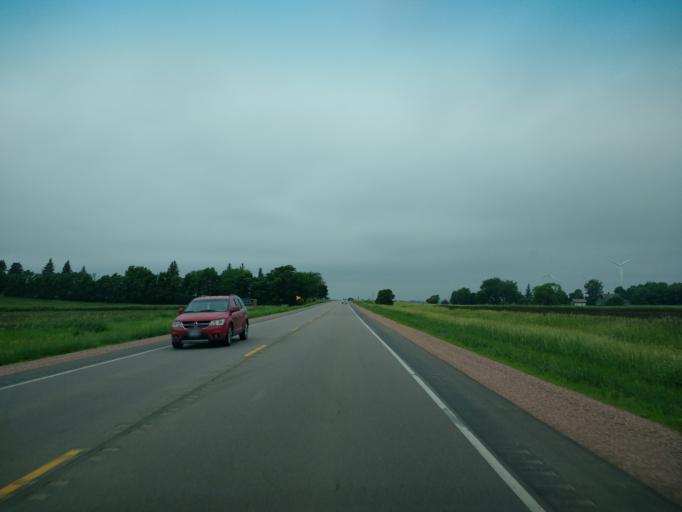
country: US
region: Iowa
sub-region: O'Brien County
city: Sanborn
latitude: 43.1861
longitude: -95.6771
